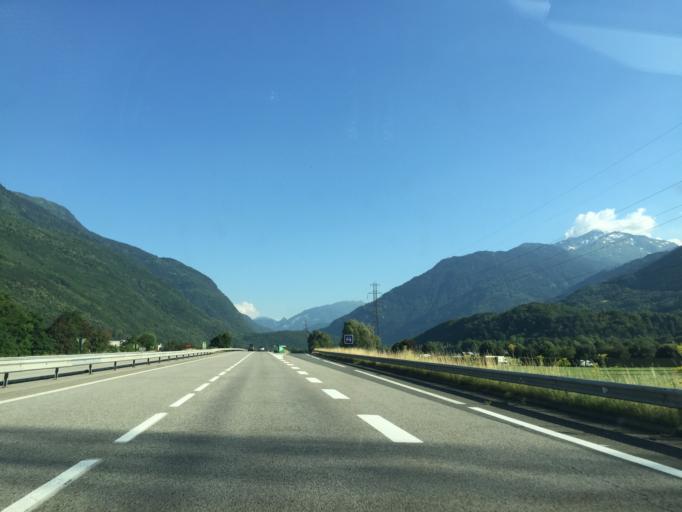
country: FR
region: Rhone-Alpes
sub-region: Departement de la Savoie
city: La Bathie
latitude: 45.6314
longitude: 6.4434
